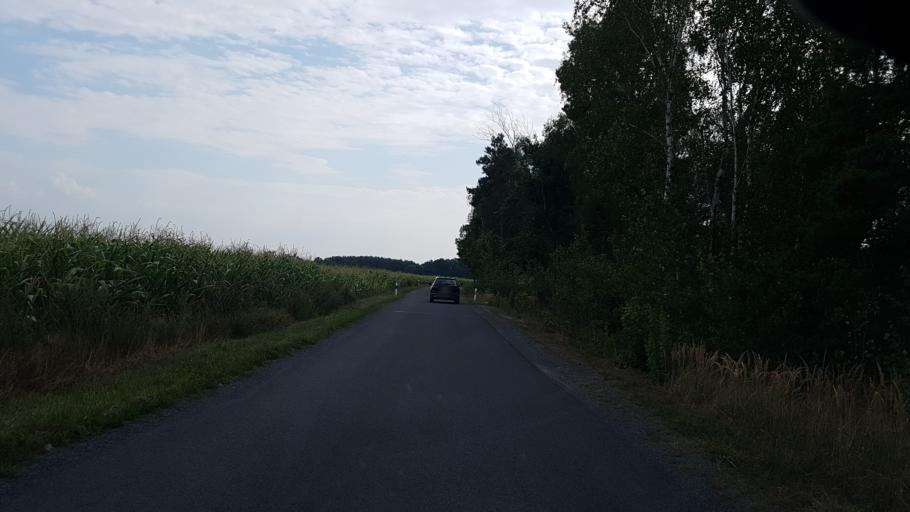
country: DE
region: Brandenburg
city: Plessa
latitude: 51.5134
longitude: 13.6793
